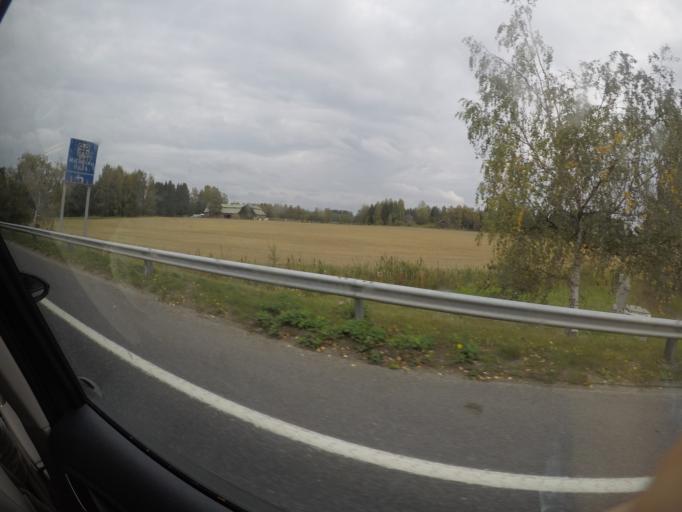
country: FI
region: Haeme
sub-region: Haemeenlinna
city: Parola
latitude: 61.0604
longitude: 24.3924
